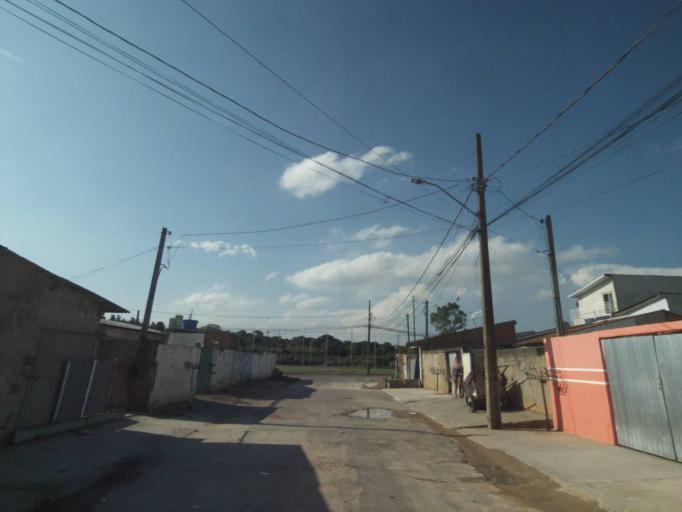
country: BR
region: Parana
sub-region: Araucaria
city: Araucaria
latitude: -25.5284
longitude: -49.3394
